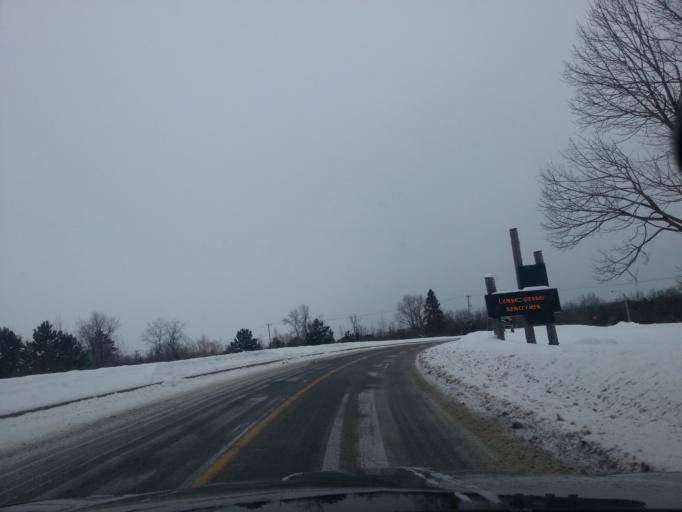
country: CA
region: Ontario
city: Ottawa
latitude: 45.4383
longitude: -75.7607
